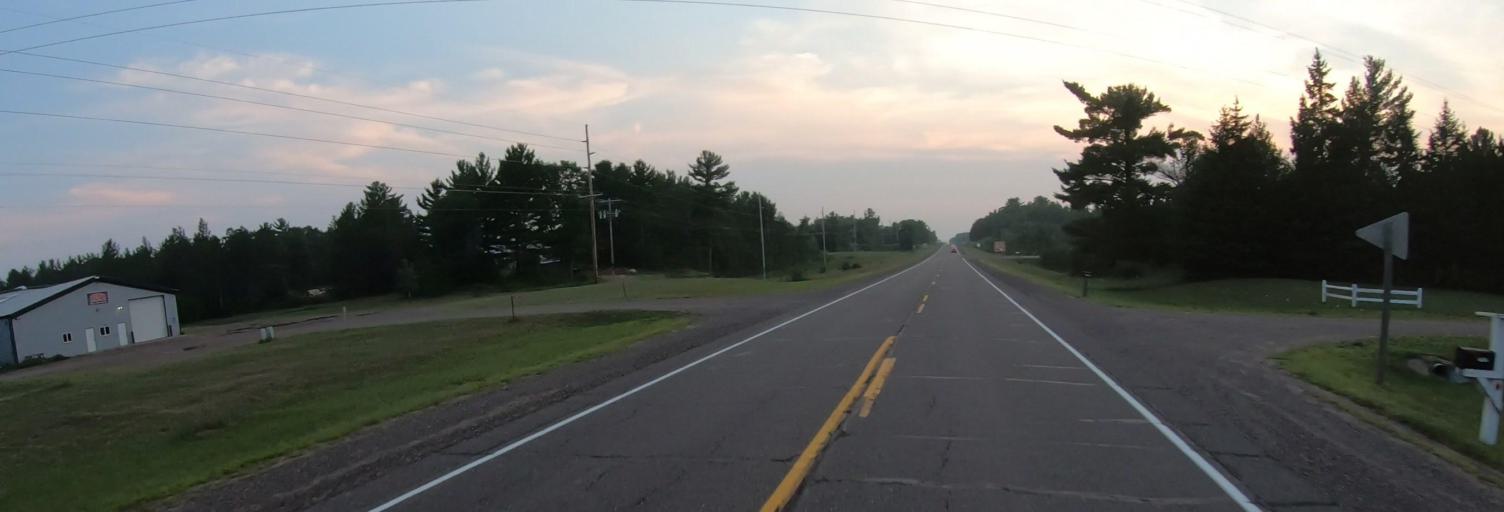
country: US
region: Wisconsin
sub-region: Burnett County
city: Grantsburg
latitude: 45.7732
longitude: -92.7207
